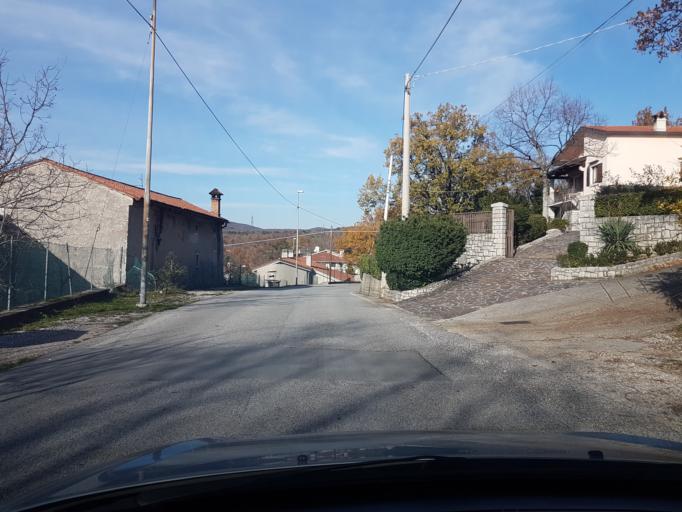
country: IT
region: Friuli Venezia Giulia
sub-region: Provincia di Trieste
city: Sistiana-Visogliano
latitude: 45.7757
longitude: 13.6466
